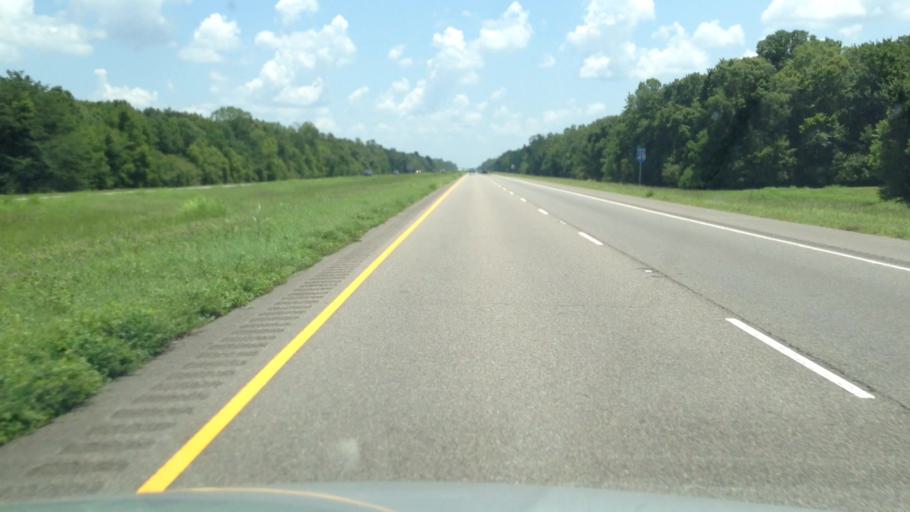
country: US
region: Louisiana
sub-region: Avoyelles Parish
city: Bunkie
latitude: 30.9817
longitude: -92.3011
